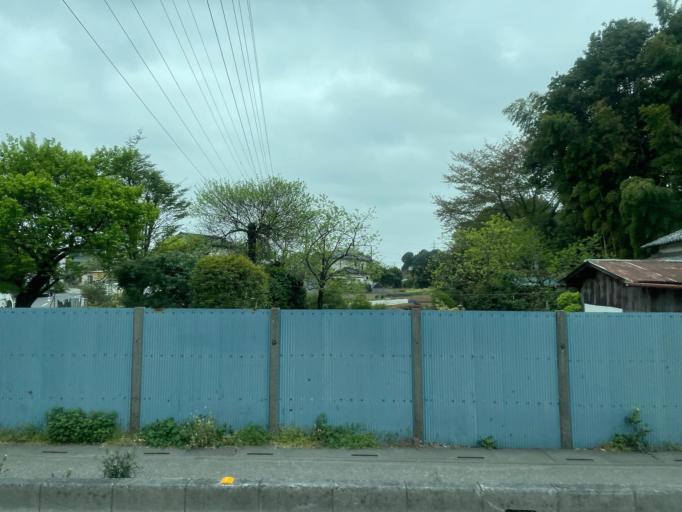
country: JP
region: Saitama
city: Iwatsuki
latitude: 35.9222
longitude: 139.7167
